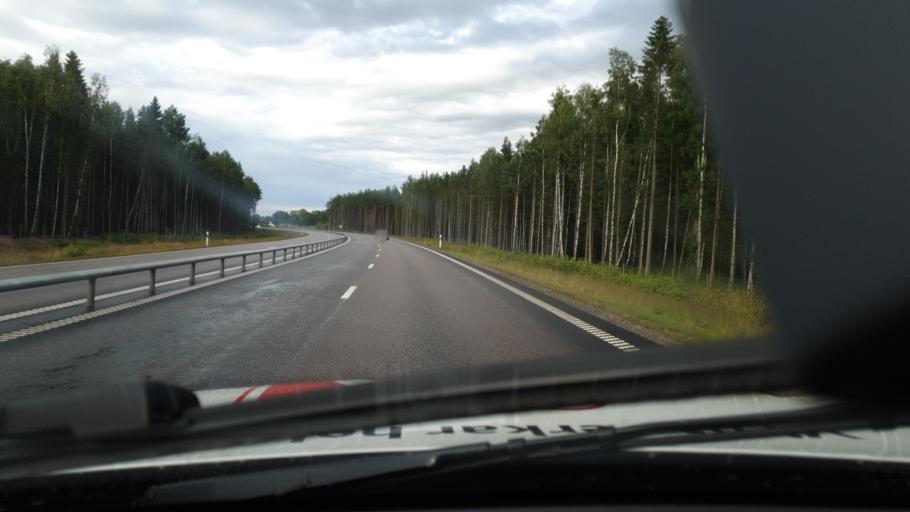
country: SE
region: Vaestra Goetaland
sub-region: Lidkopings Kommun
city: Vinninga
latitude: 58.4799
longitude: 13.2695
